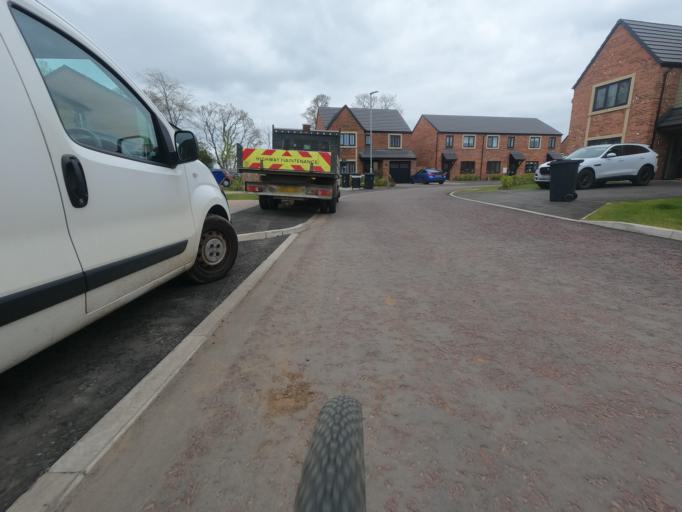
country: GB
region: England
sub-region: Northumberland
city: Ponteland
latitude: 55.0600
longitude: -1.7563
